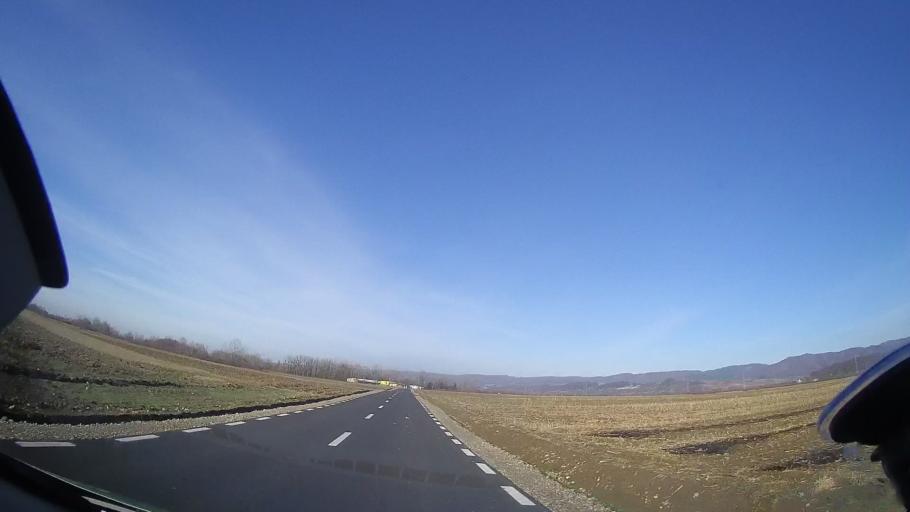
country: RO
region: Bihor
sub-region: Comuna Vadu Crisului
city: Vadu Crisului
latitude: 46.9984
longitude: 22.5050
